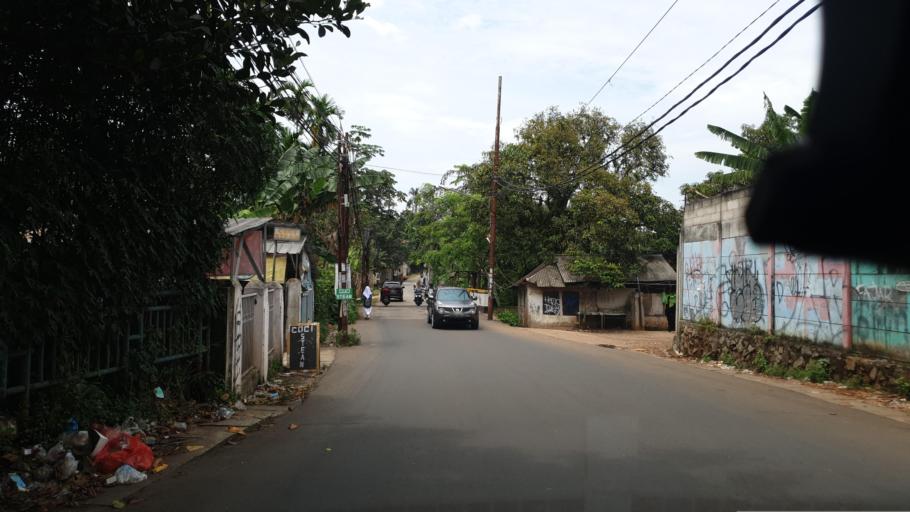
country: ID
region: West Java
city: Pamulang
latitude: -6.3666
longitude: 106.7529
